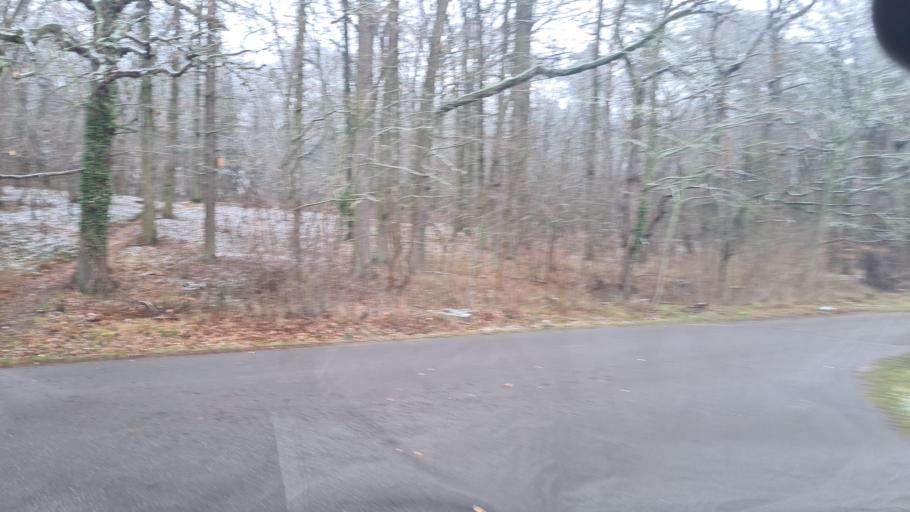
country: DE
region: Brandenburg
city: Munchehofe
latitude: 52.1450
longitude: 13.8382
